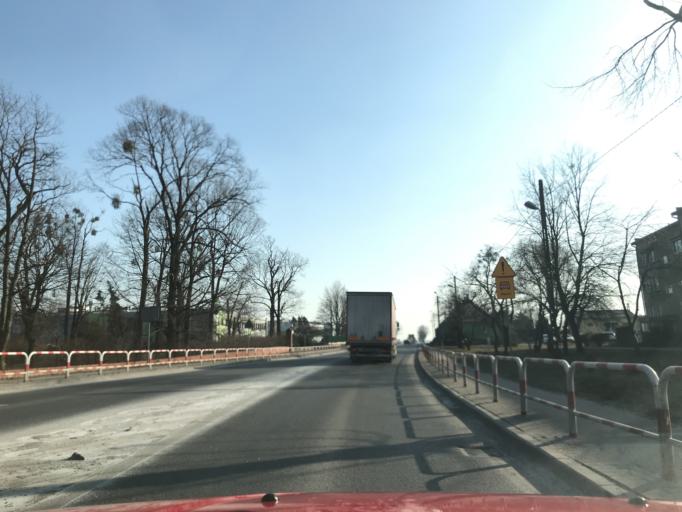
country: PL
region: Greater Poland Voivodeship
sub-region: Powiat sredzki
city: Nowe Miasto nad Warta
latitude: 52.0746
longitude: 17.4204
